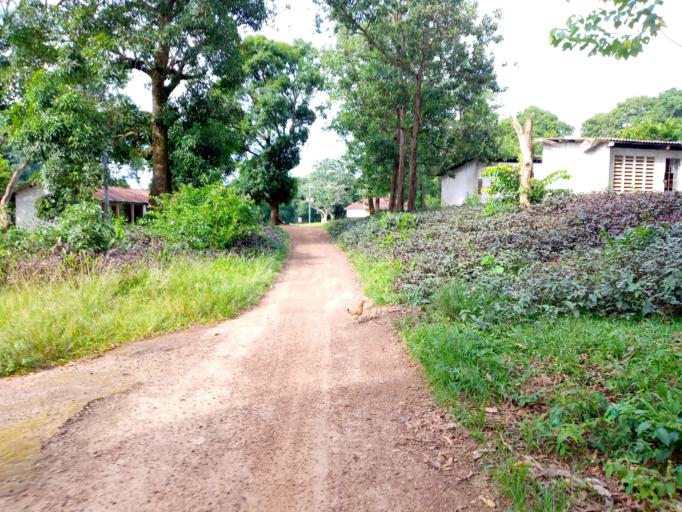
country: SL
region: Northern Province
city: Magburaka
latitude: 8.7194
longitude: -11.9448
